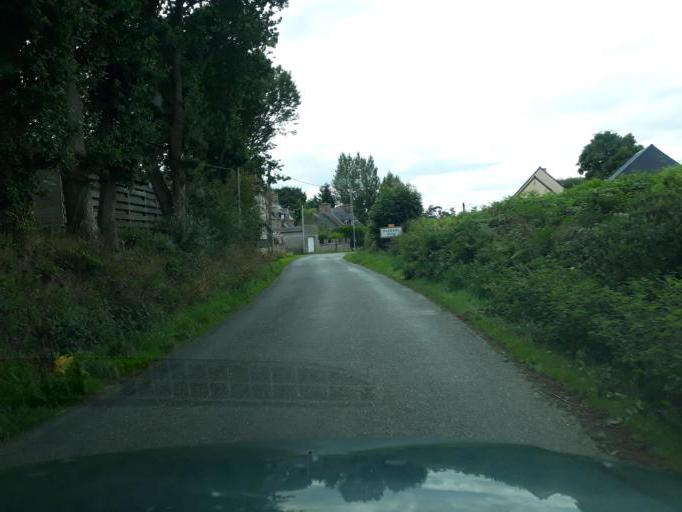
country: FR
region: Brittany
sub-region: Departement des Cotes-d'Armor
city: Plehedel
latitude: 48.6688
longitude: -2.9867
